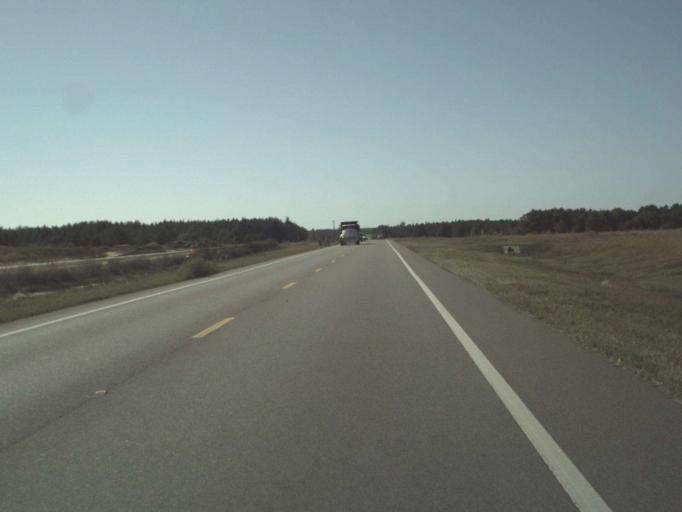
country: US
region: Florida
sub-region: Walton County
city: Freeport
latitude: 30.5398
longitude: -86.1075
